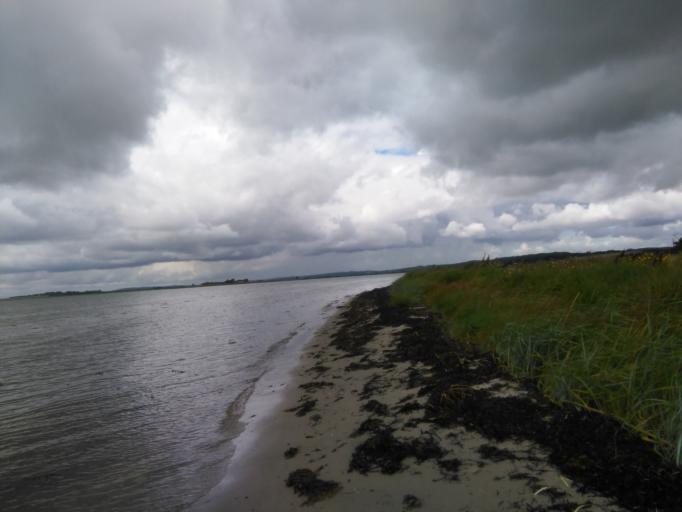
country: DK
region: Central Jutland
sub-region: Odder Kommune
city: Odder
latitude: 55.8571
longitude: 10.1425
